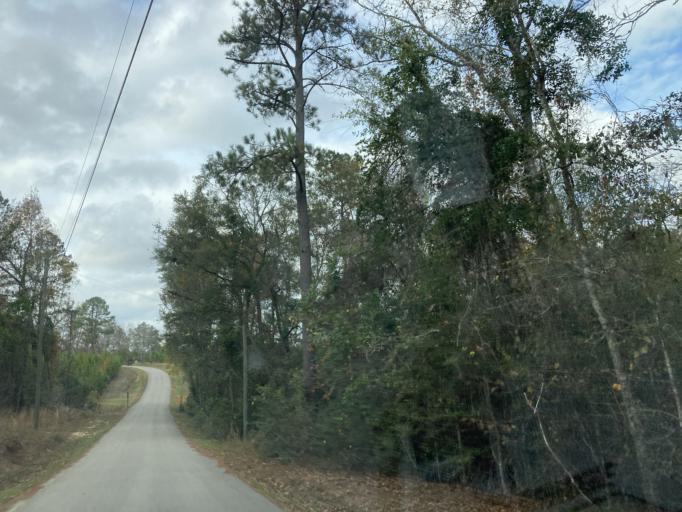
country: US
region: Mississippi
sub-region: Lamar County
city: Purvis
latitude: 31.1851
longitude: -89.5785
